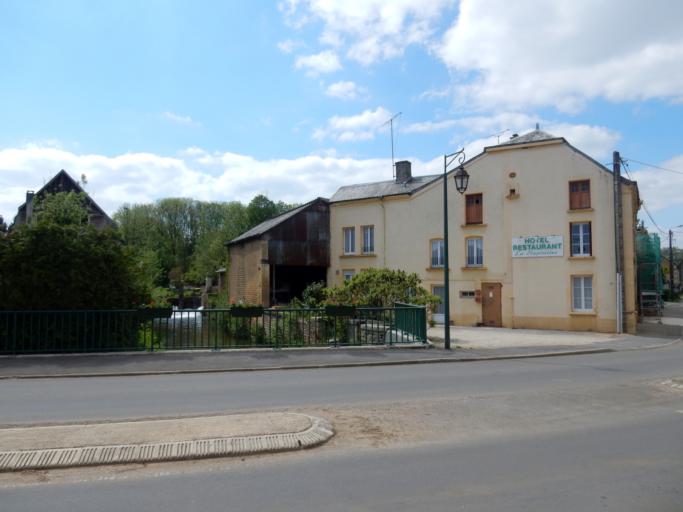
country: FR
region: Champagne-Ardenne
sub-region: Departement des Ardennes
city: Bazeilles
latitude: 49.6528
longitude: 4.9939
